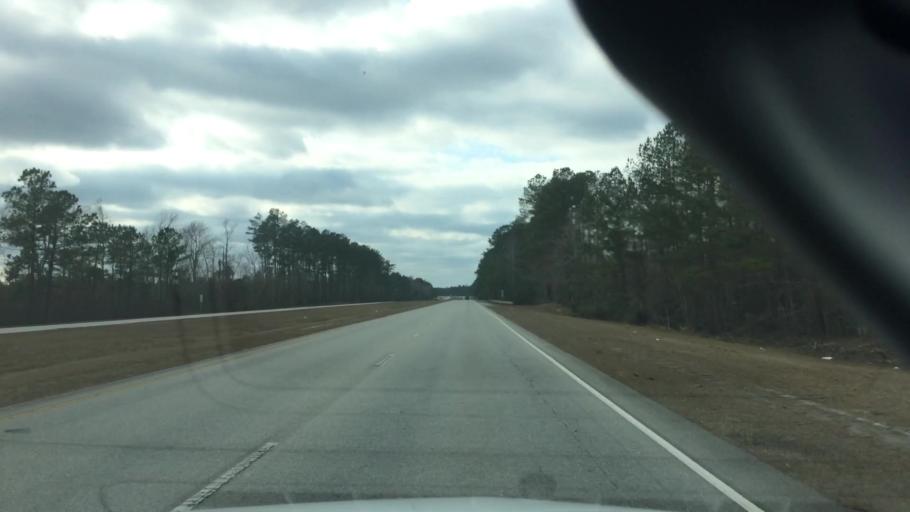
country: US
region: North Carolina
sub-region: Brunswick County
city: Bolivia
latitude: 34.0665
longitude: -78.1849
